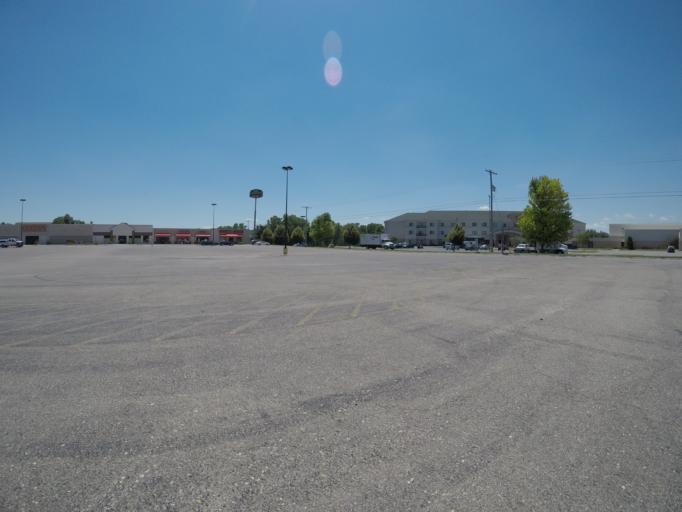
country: US
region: Kansas
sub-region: Geary County
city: Junction City
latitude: 39.0204
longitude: -96.8226
